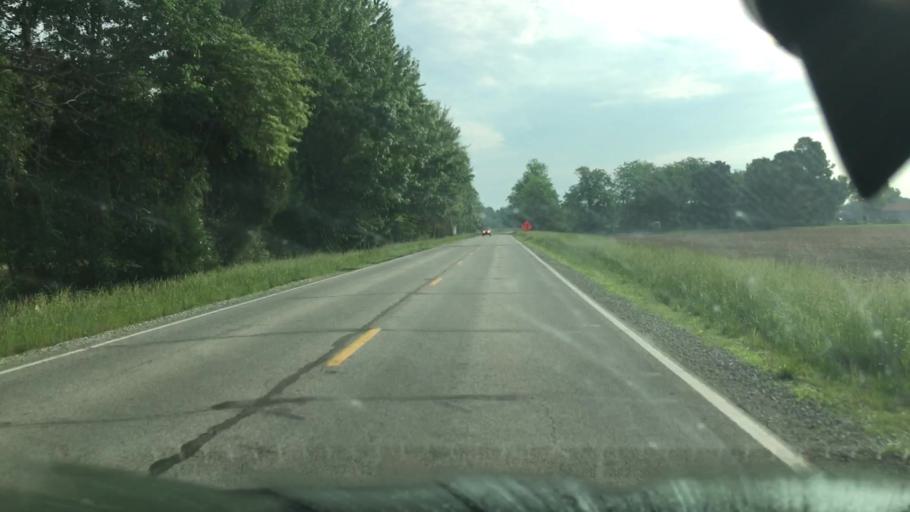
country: US
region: Kentucky
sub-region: Hancock County
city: Lewisport
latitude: 37.9435
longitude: -86.9754
